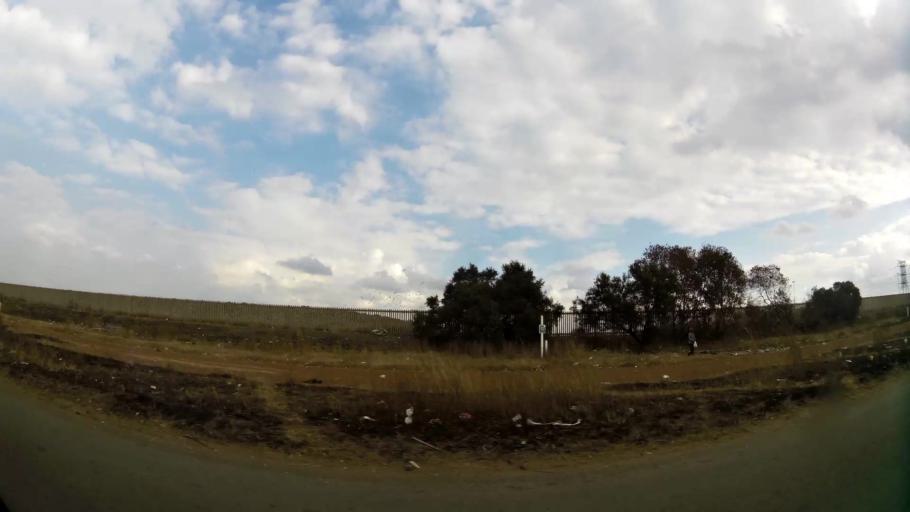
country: ZA
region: Gauteng
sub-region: Sedibeng District Municipality
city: Vanderbijlpark
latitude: -26.6647
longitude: 27.8588
